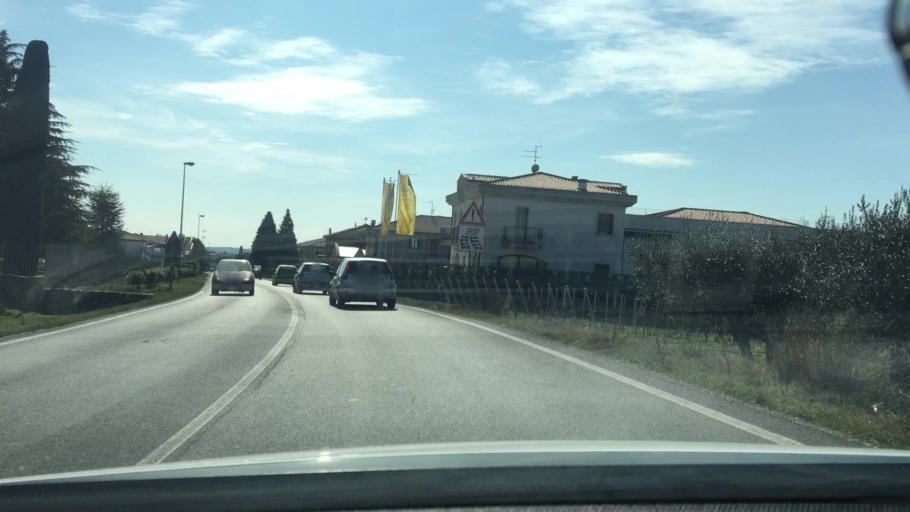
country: IT
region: Veneto
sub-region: Provincia di Verona
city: Cellore
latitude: 45.4906
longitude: 11.1751
